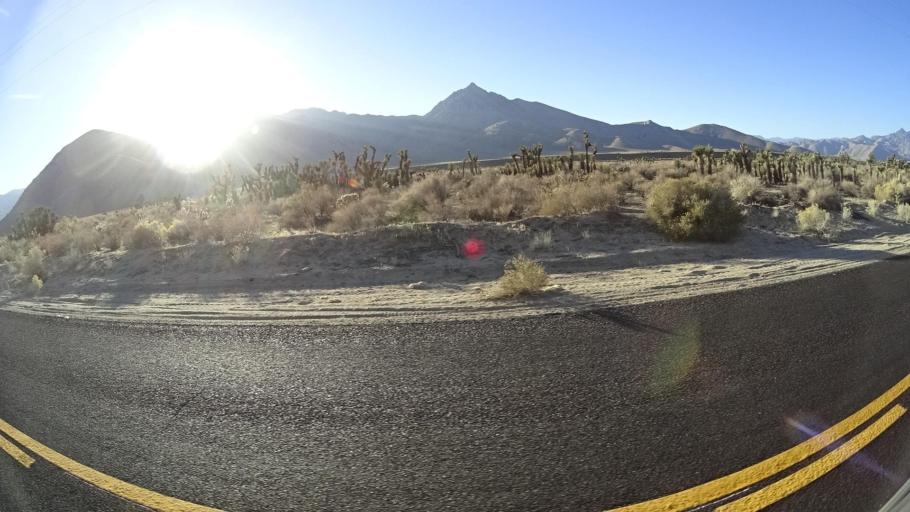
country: US
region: California
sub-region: Kern County
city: Weldon
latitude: 35.6211
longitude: -118.2432
